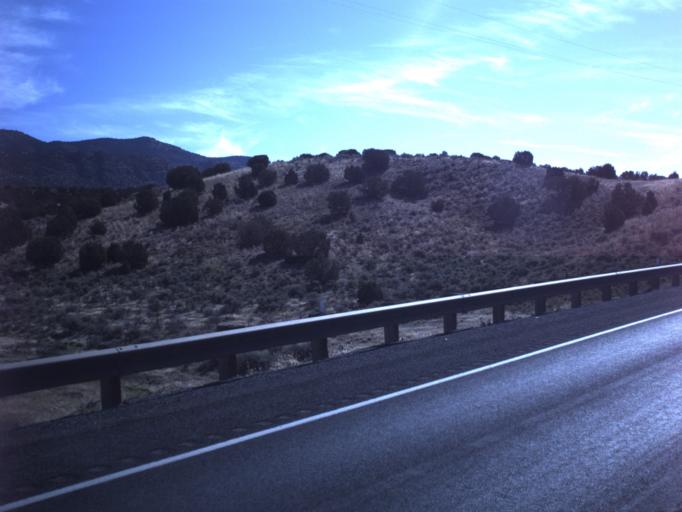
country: US
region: Utah
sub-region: Sanpete County
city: Gunnison
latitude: 39.2843
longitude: -111.8820
